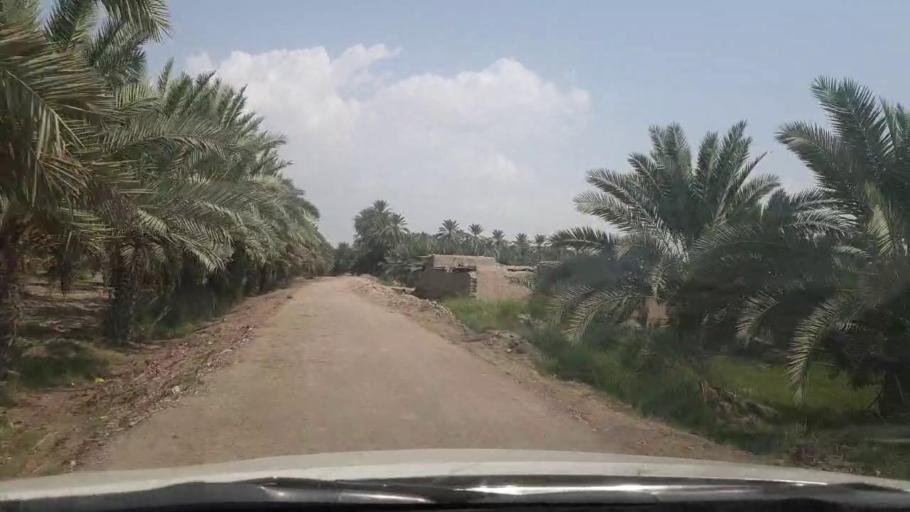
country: PK
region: Sindh
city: Khairpur
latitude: 27.5537
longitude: 68.8442
